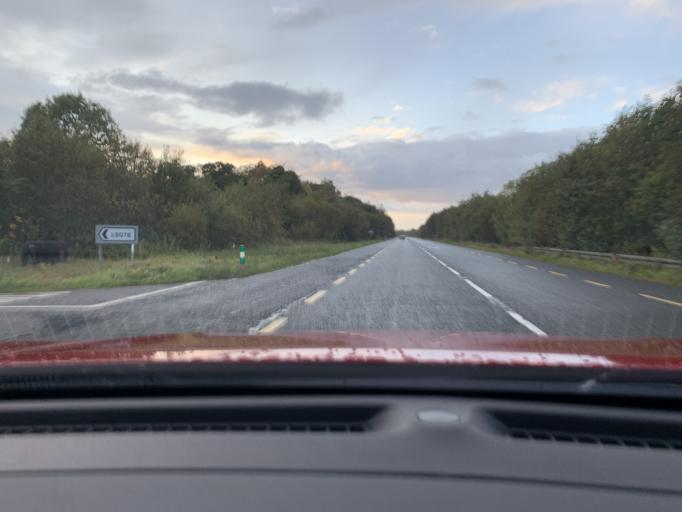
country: IE
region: Connaught
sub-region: County Leitrim
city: Carrick-on-Shannon
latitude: 53.9517
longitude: -8.1519
